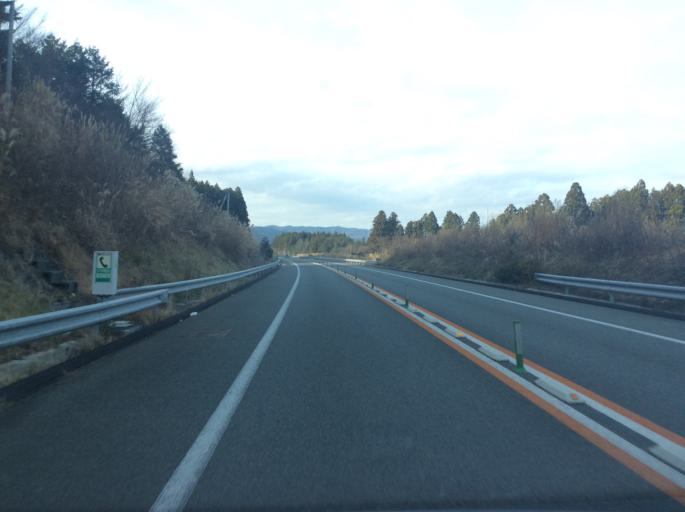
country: JP
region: Fukushima
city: Namie
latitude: 37.3478
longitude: 140.9859
